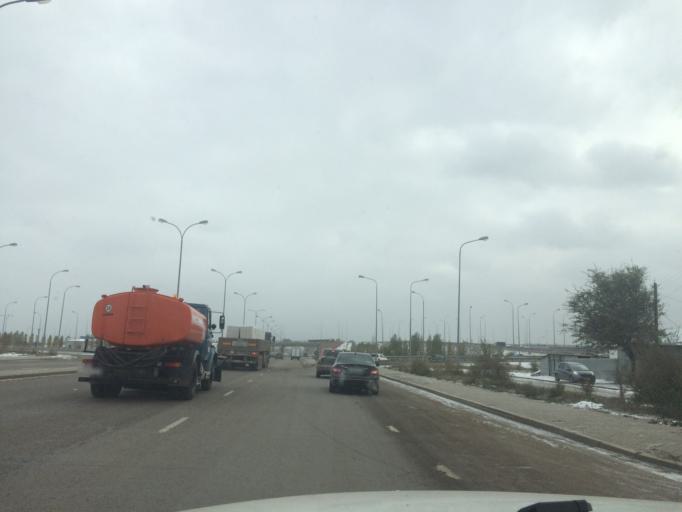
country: KZ
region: Astana Qalasy
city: Astana
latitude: 51.1752
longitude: 71.4784
